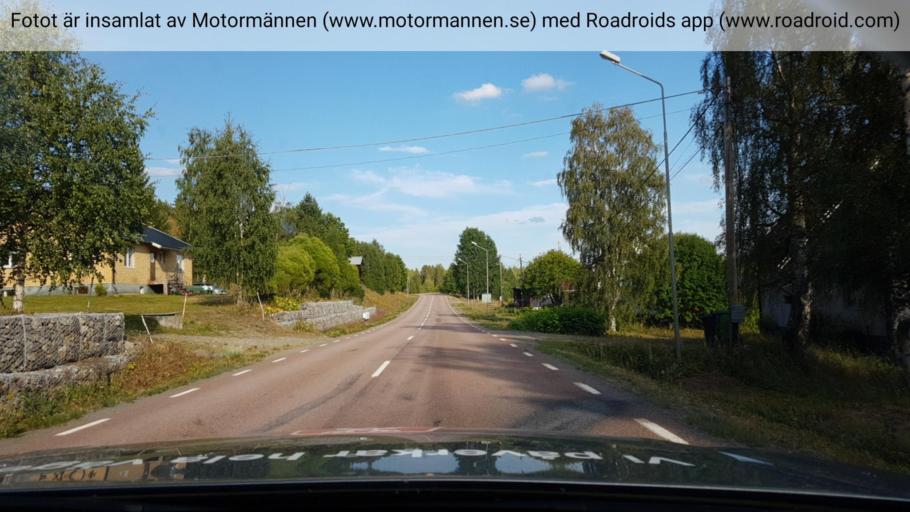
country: SE
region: Vaesternorrland
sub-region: Solleftea Kommun
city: As
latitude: 63.5941
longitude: 16.1768
